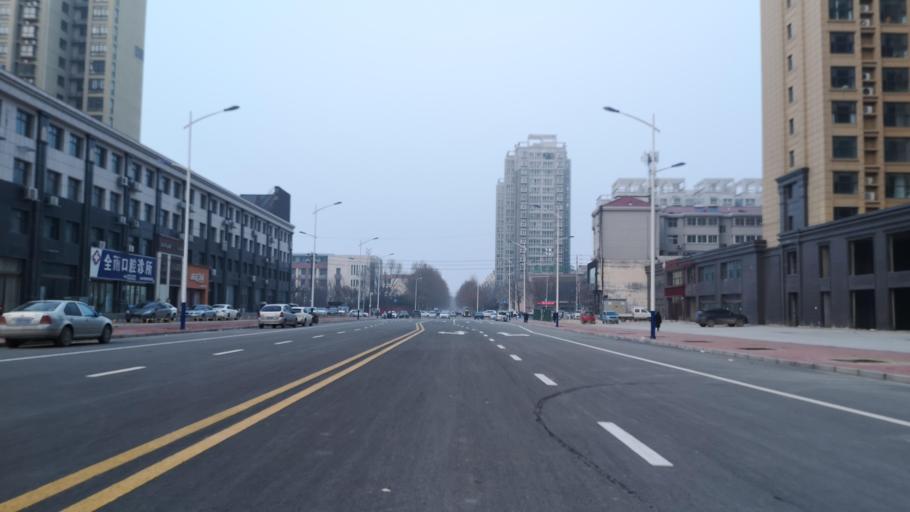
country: CN
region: Henan Sheng
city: Zhongyuanlu
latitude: 35.7518
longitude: 115.0603
